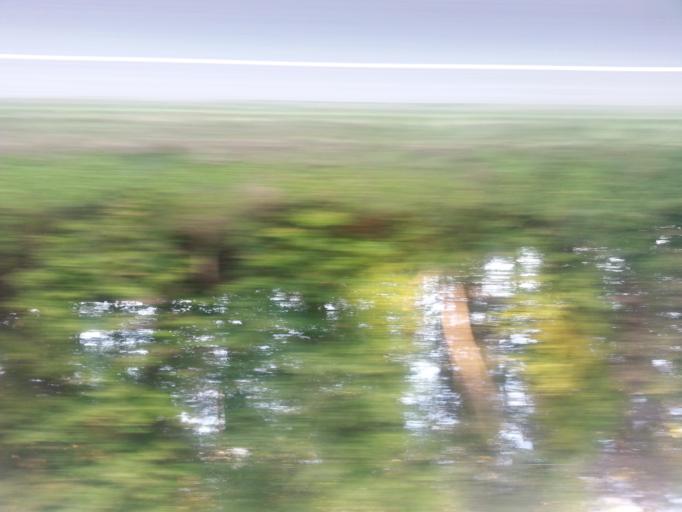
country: US
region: Tennessee
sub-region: Anderson County
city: Norris
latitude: 36.1878
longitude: -84.0998
